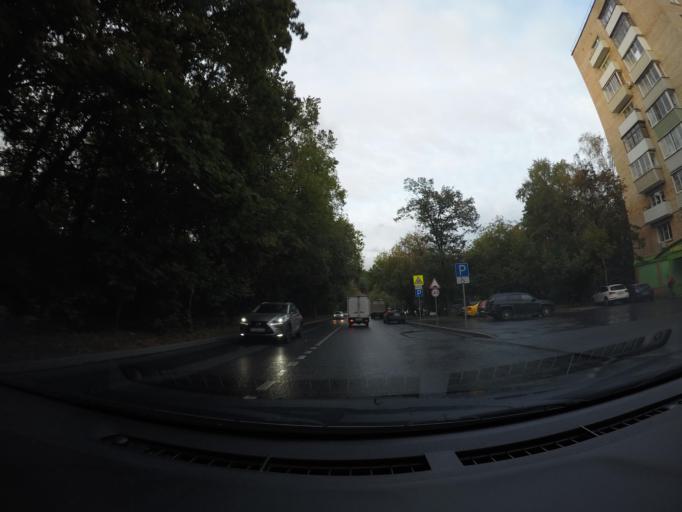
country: RU
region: Moscow
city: Sokol'niki
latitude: 55.7991
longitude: 37.6893
